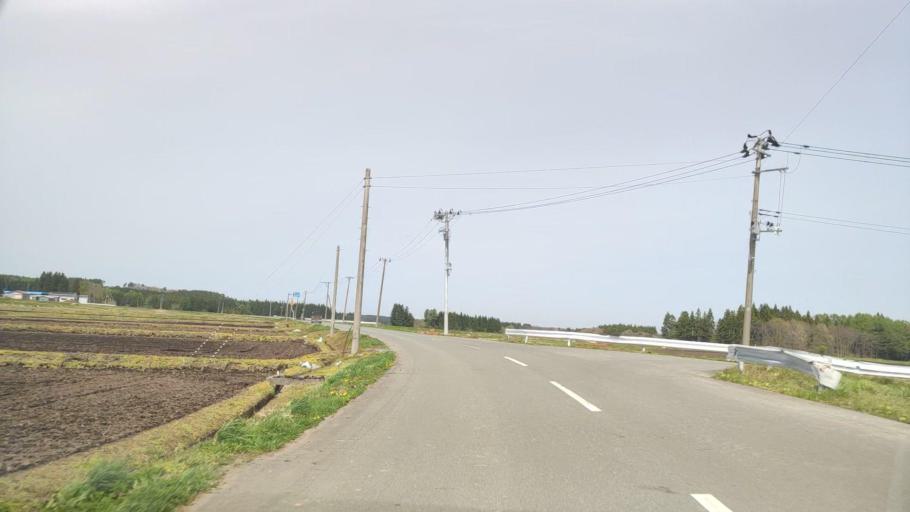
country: JP
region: Aomori
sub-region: Misawa Shi
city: Inuotose
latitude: 40.7599
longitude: 141.1193
